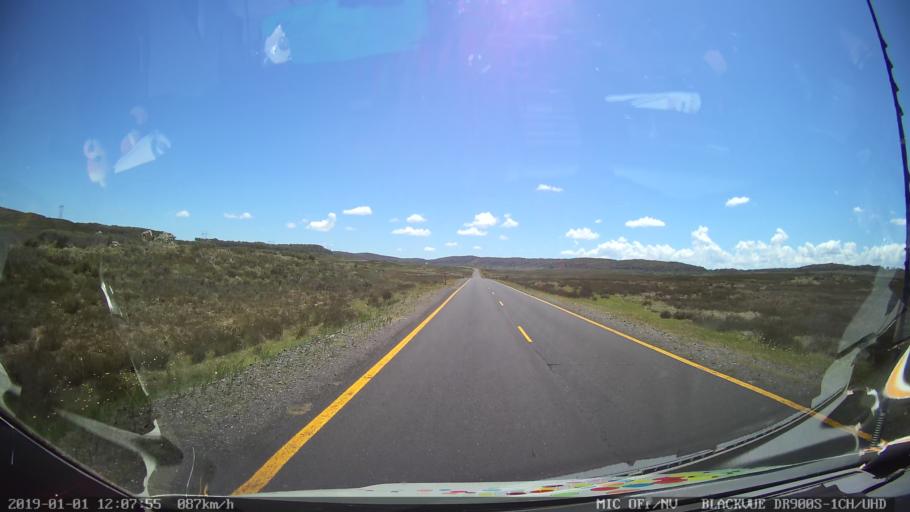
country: AU
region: New South Wales
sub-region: Tumut Shire
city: Tumut
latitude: -35.8269
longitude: 148.4921
